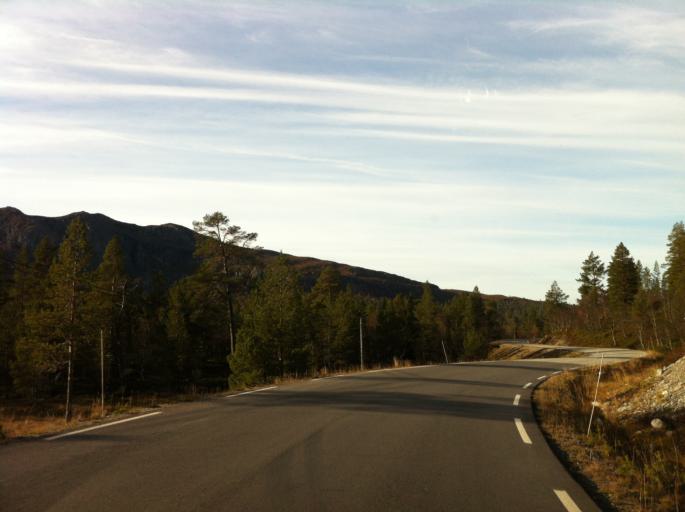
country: NO
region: Hedmark
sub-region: Engerdal
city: Engerdal
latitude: 62.0902
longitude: 12.0479
